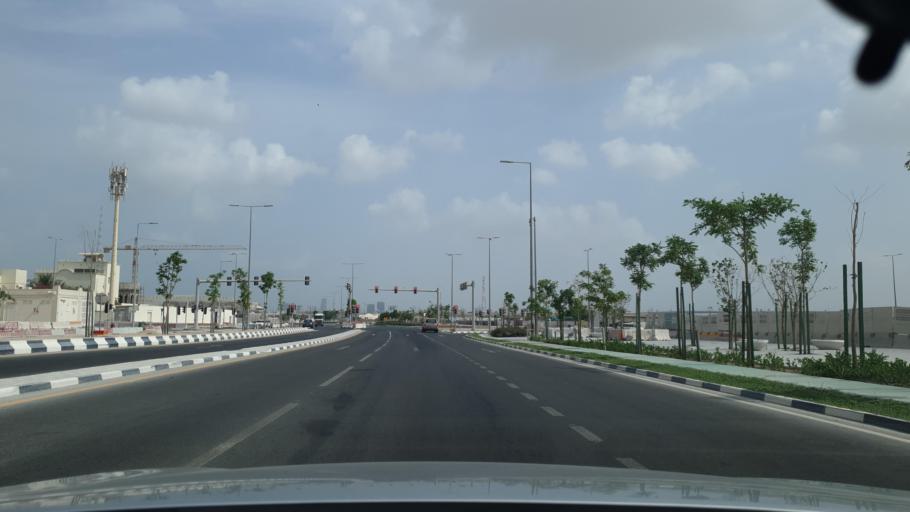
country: QA
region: Baladiyat ar Rayyan
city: Ar Rayyan
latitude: 25.2773
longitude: 51.4595
